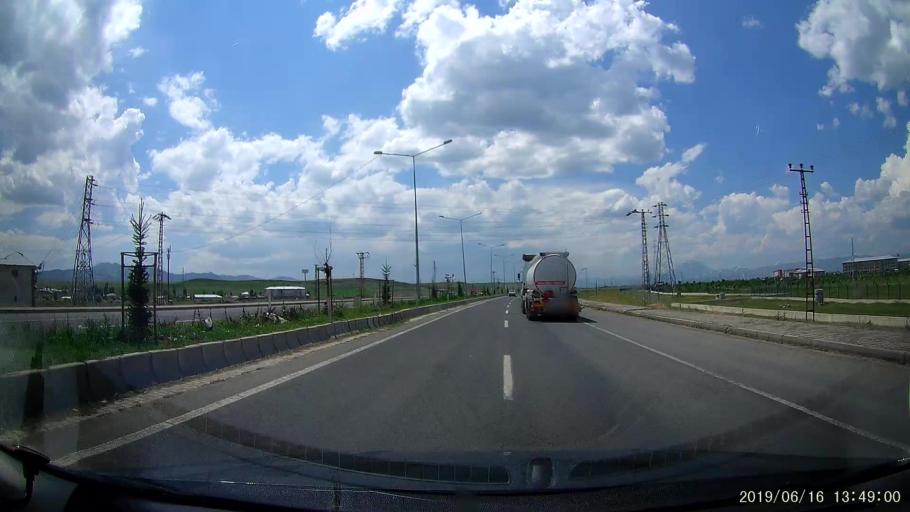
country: TR
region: Agri
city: Agri
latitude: 39.7150
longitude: 42.9971
